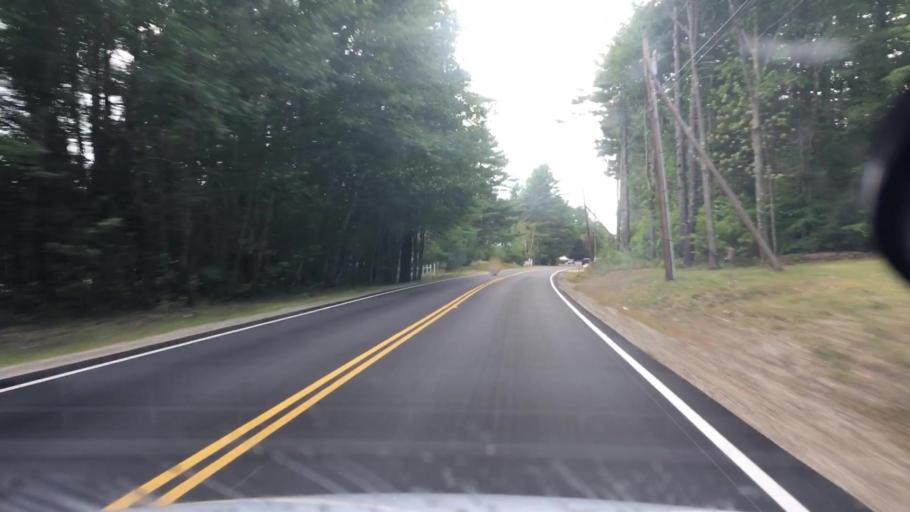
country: US
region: New Hampshire
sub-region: Carroll County
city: Sanbornville
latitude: 43.5343
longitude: -71.0245
